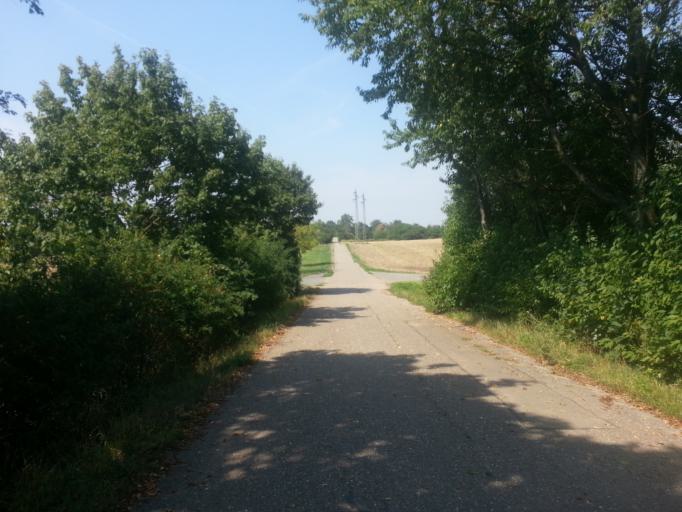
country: DE
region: Baden-Wuerttemberg
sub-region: Karlsruhe Region
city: Ilvesheim
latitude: 49.4558
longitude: 8.5744
